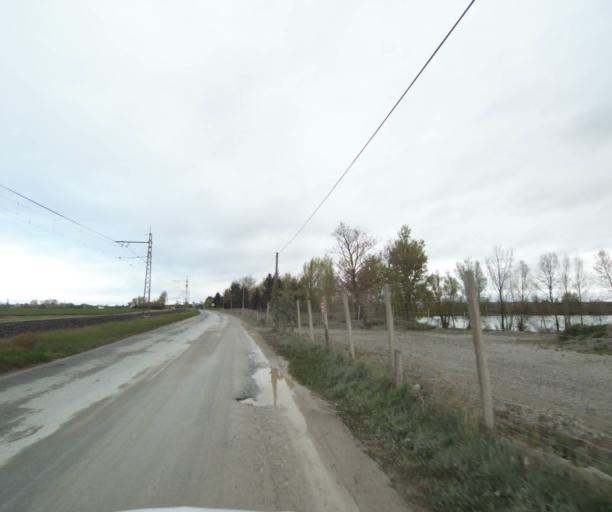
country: FR
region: Midi-Pyrenees
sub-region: Departement de l'Ariege
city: Saverdun
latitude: 43.2256
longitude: 1.6100
